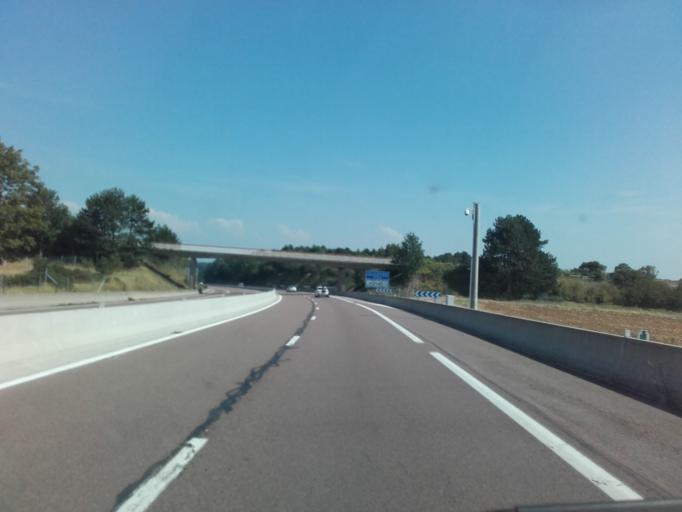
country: FR
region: Bourgogne
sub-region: Departement de la Cote-d'Or
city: Savigny-les-Beaune
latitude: 47.0594
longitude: 4.7766
